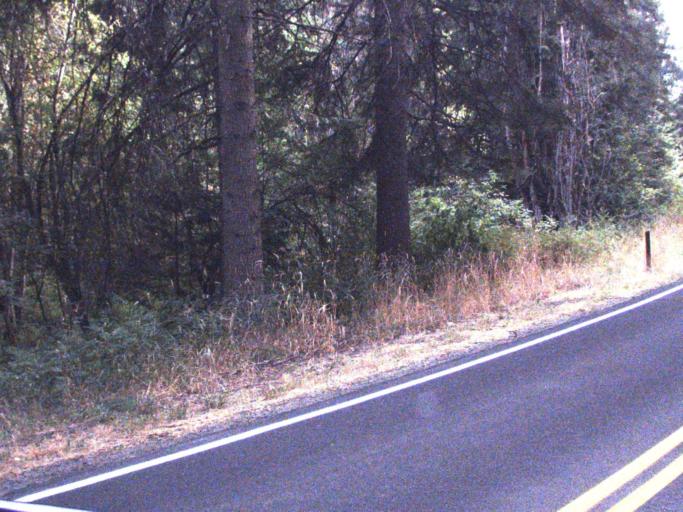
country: US
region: Washington
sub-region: Spokane County
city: Trentwood
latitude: 47.8630
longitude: -117.1625
